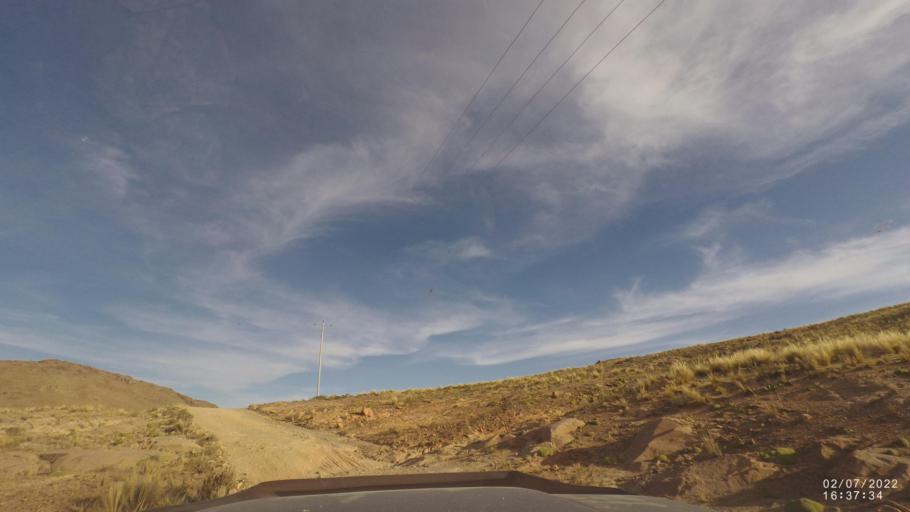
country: BO
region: Cochabamba
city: Irpa Irpa
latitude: -17.9670
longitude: -66.4976
